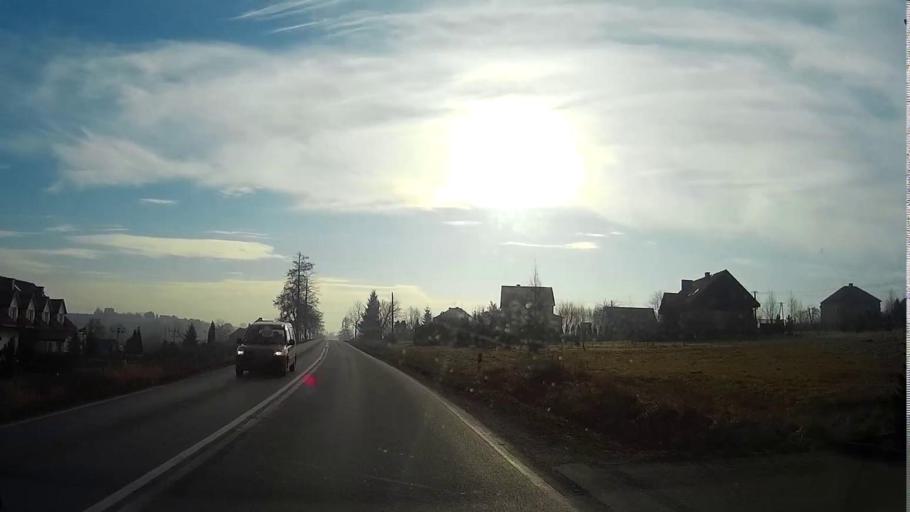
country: PL
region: Lesser Poland Voivodeship
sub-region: Powiat chrzanowski
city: Brodla
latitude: 50.0498
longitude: 19.5681
